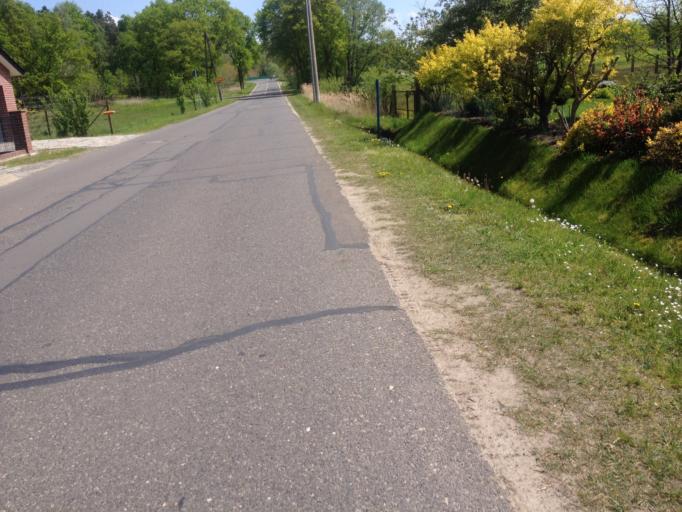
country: DE
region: Brandenburg
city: Drehnow
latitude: 51.8254
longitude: 14.3475
